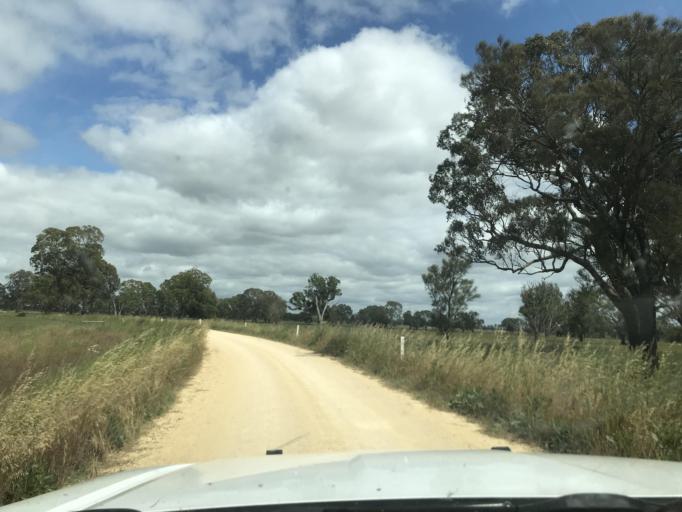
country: AU
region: South Australia
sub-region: Naracoorte and Lucindale
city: Naracoorte
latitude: -37.0062
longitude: 141.1133
